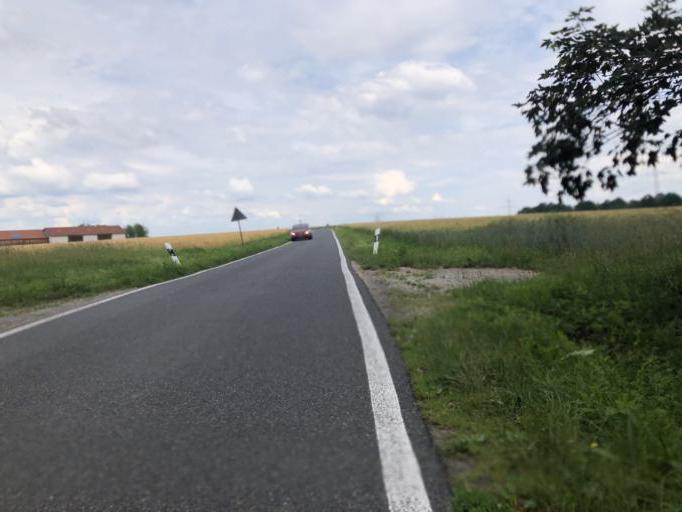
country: DE
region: Bavaria
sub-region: Regierungsbezirk Mittelfranken
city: Obermichelbach
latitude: 49.5738
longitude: 10.9358
